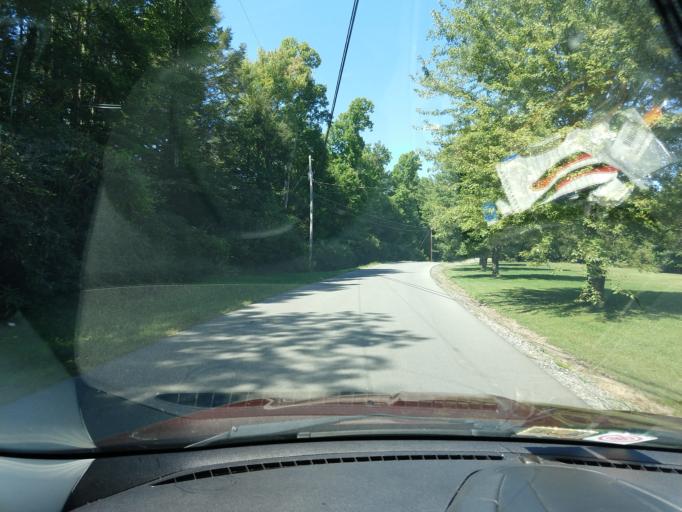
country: US
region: West Virginia
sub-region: Nicholas County
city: Craigsville
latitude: 38.2742
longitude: -80.7131
